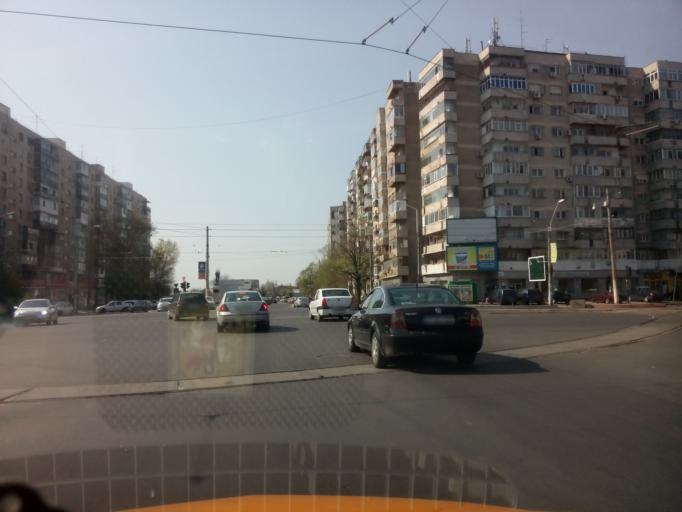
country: RO
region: Ilfov
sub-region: Comuna Popesti-Leordeni
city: Popesti-Leordeni
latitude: 44.4134
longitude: 26.1638
